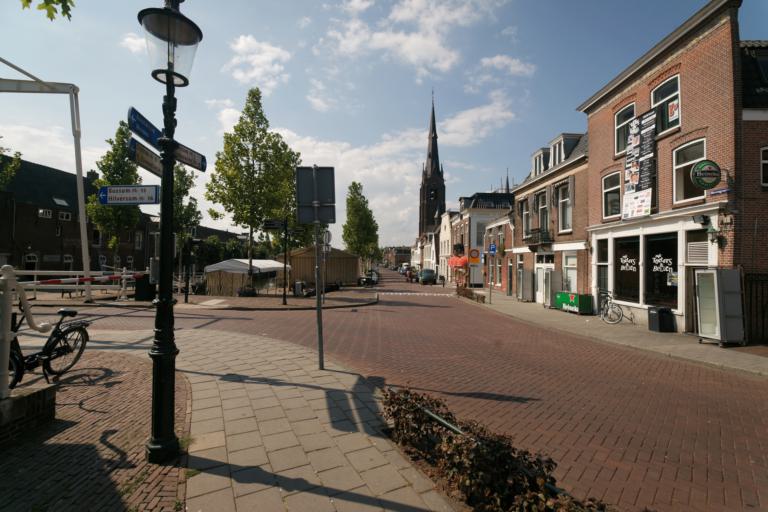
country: NL
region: North Holland
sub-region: Gemeente Weesp
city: Weesp
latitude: 52.3091
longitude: 5.0429
